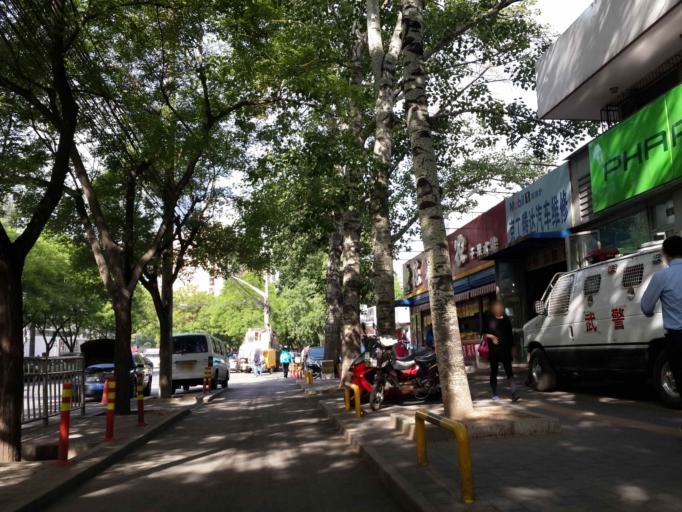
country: CN
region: Beijing
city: Chaowai
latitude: 39.9278
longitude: 116.4593
